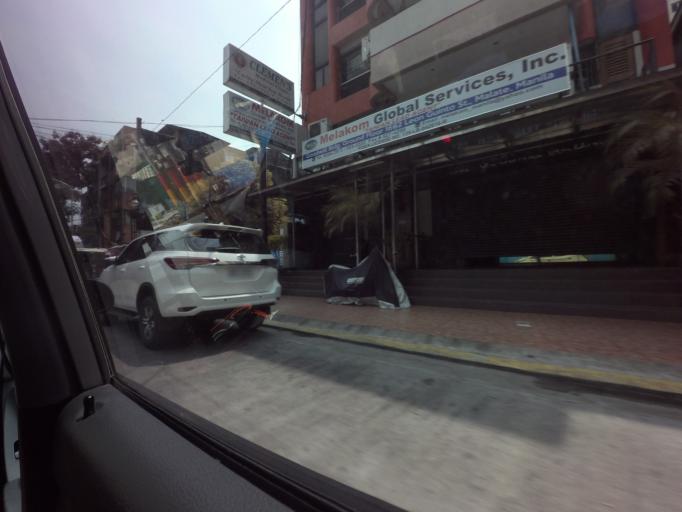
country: PH
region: Metro Manila
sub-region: City of Manila
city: Port Area
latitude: 14.5756
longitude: 120.9897
